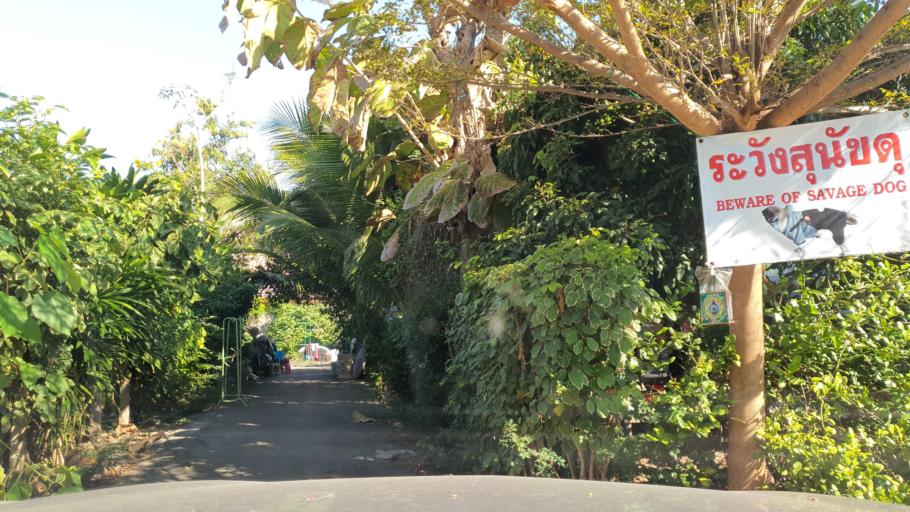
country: TH
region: Chiang Mai
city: Hang Dong
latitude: 18.6960
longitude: 98.9367
